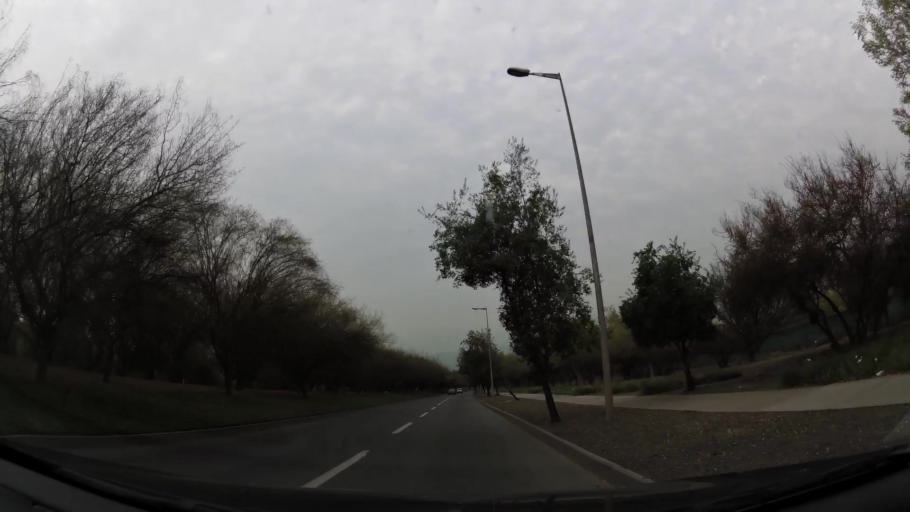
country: CL
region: Santiago Metropolitan
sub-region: Provincia de Chacabuco
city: Chicureo Abajo
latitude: -33.2824
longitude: -70.6405
